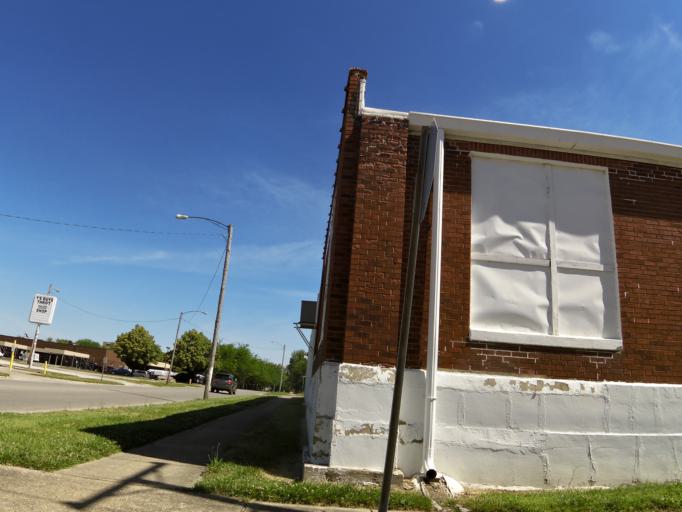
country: US
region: Illinois
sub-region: Vermilion County
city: Danville
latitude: 40.1283
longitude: -87.6272
